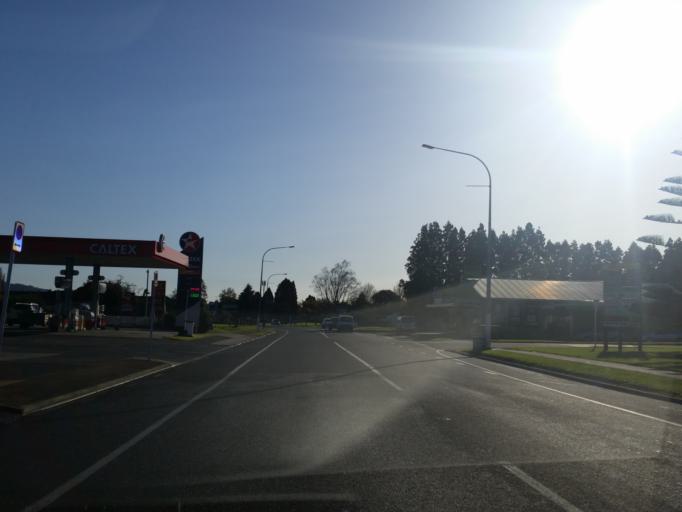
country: NZ
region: Bay of Plenty
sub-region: Western Bay of Plenty District
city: Katikati
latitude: -37.5582
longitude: 175.9163
